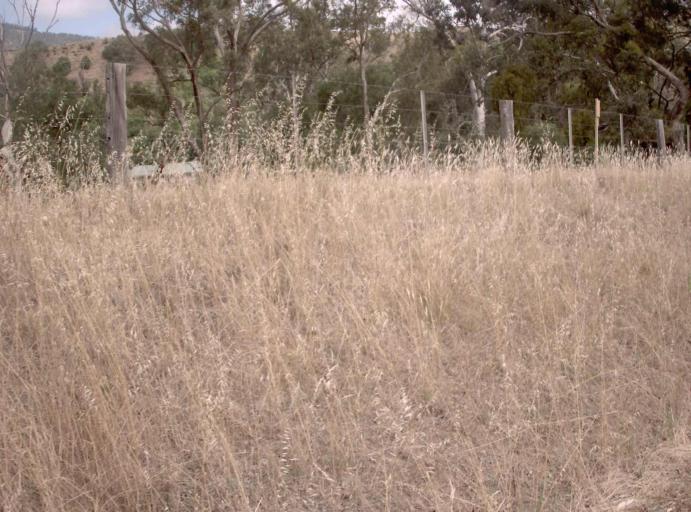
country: AU
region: Victoria
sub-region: Wellington
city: Heyfield
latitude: -37.6307
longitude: 146.6232
